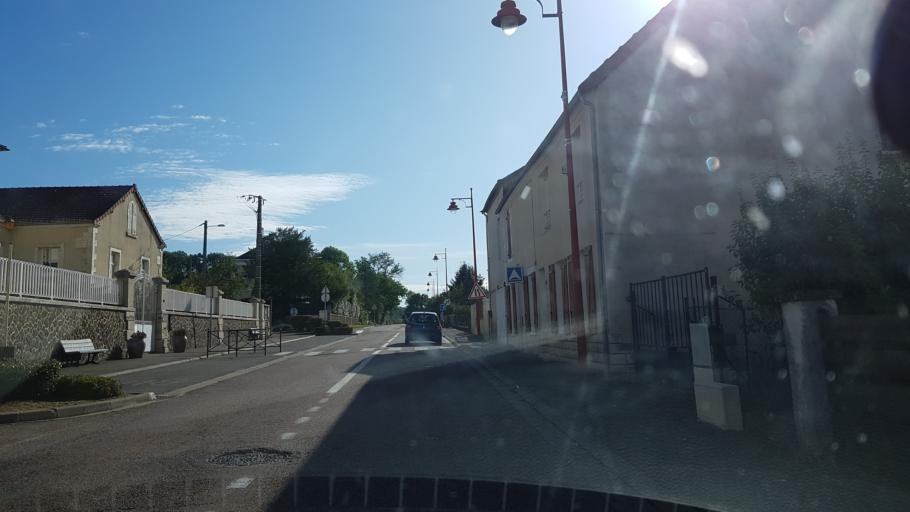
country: FR
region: Bourgogne
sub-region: Departement de la Nievre
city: Saint-Amand-en-Puisaye
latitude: 47.5408
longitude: 2.9912
